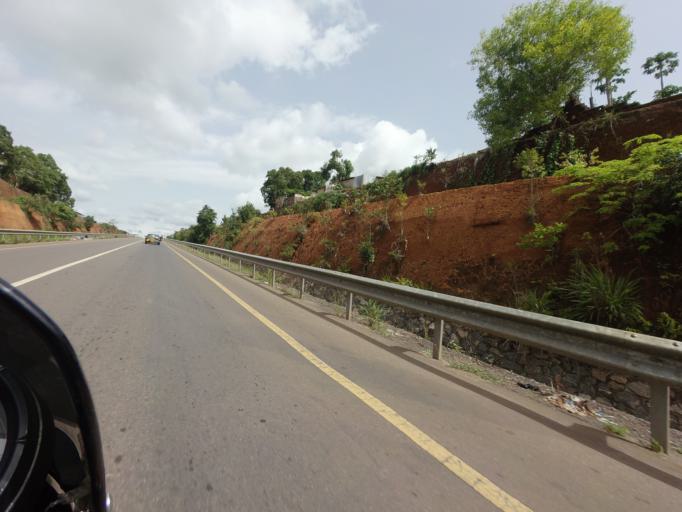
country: SL
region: Northern Province
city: Kambia
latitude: 9.1140
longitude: -12.9282
